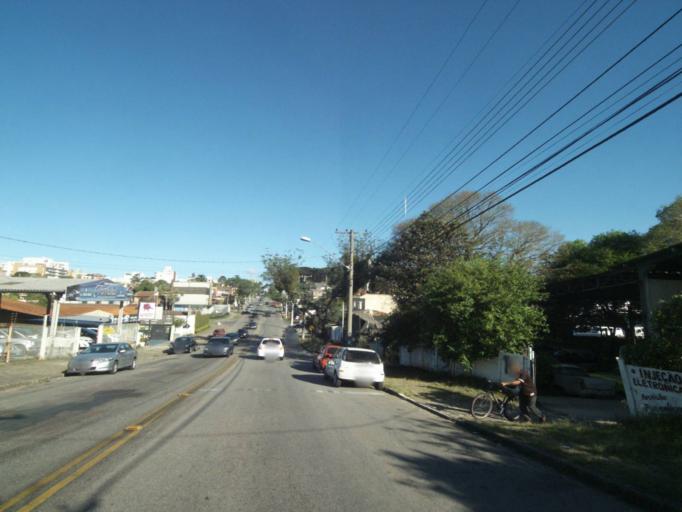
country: BR
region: Parana
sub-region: Curitiba
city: Curitiba
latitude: -25.3946
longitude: -49.2520
